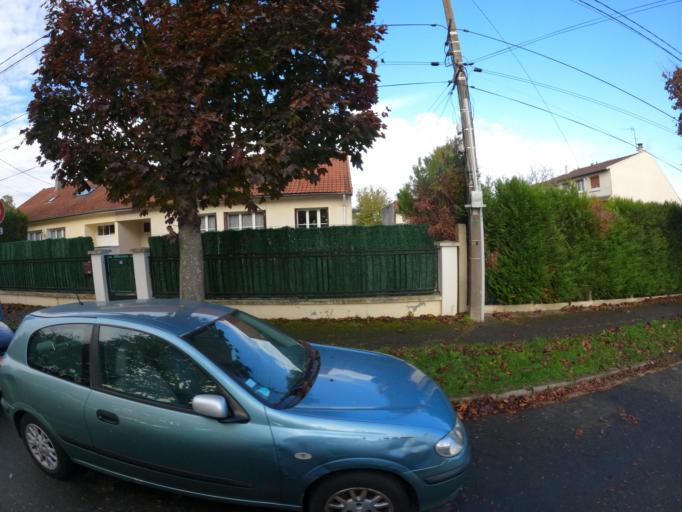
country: FR
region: Ile-de-France
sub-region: Departement de Seine-et-Marne
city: Le Pin
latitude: 48.8972
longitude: 2.6164
